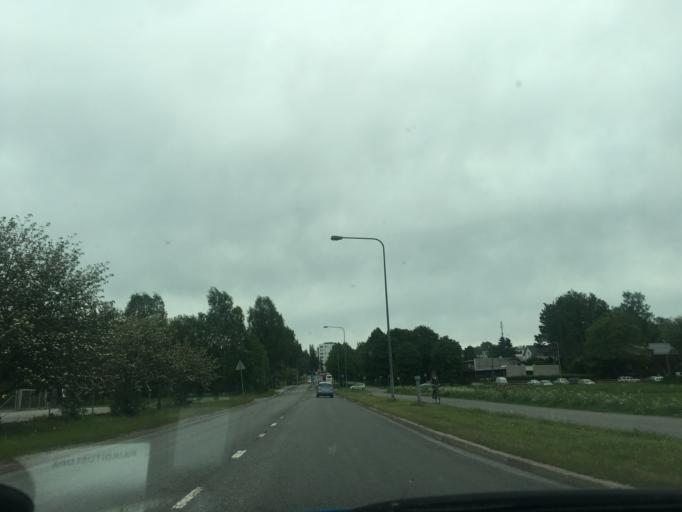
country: FI
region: Varsinais-Suomi
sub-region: Turku
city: Turku
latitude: 60.4619
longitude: 22.3049
